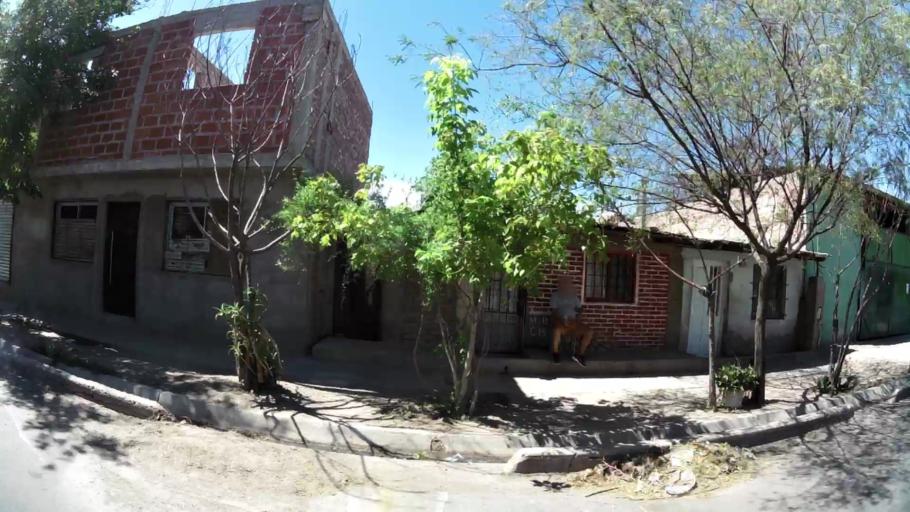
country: AR
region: Mendoza
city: Las Heras
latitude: -32.8519
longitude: -68.8711
